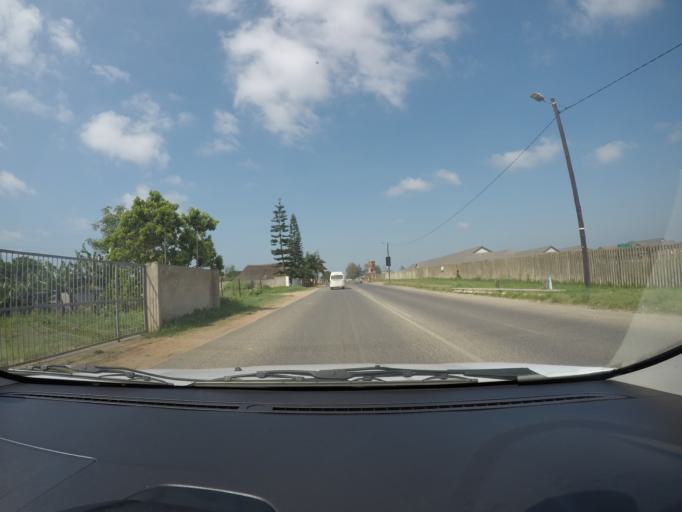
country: ZA
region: KwaZulu-Natal
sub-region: uThungulu District Municipality
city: eSikhawini
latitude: -28.8878
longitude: 31.8968
